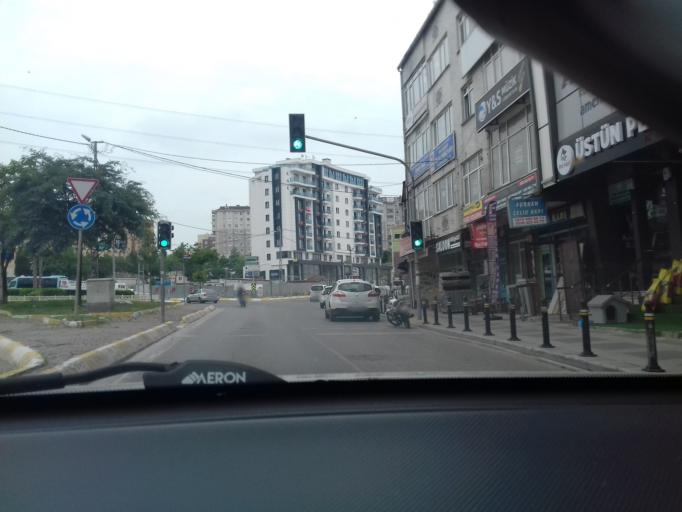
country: TR
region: Istanbul
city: Pendik
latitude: 40.9163
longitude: 29.3044
